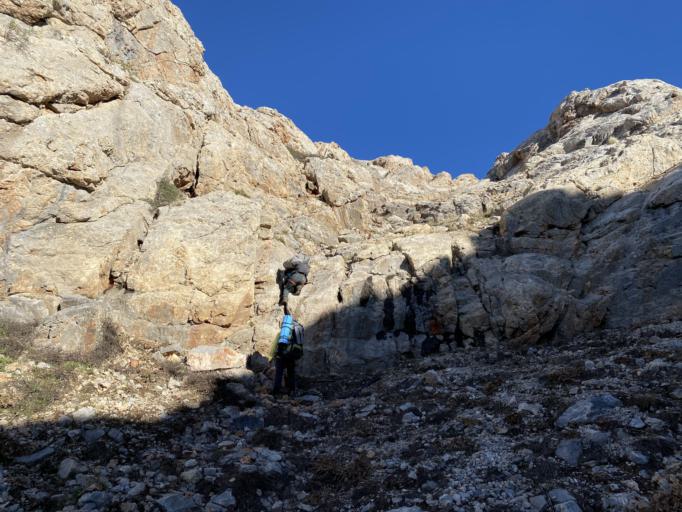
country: KZ
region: Ongtustik Qazaqstan
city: Ashchysay
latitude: 43.7641
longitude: 68.7785
